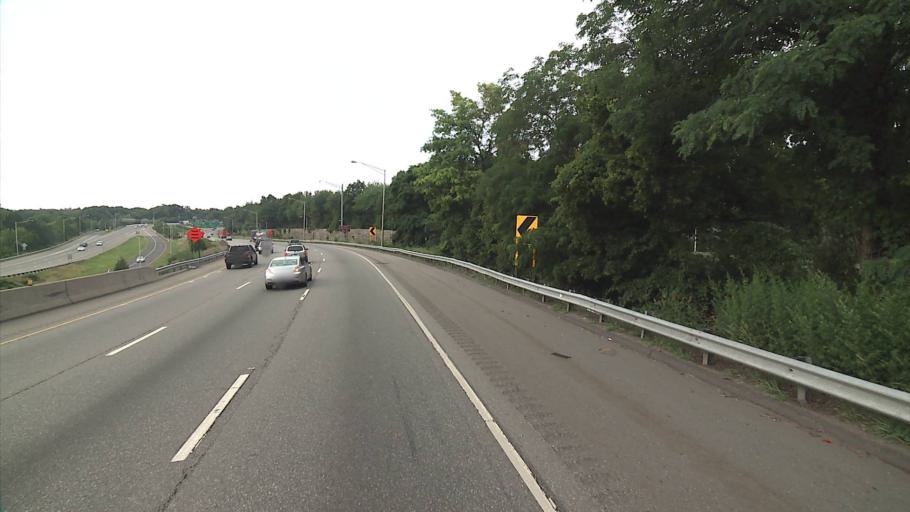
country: US
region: Connecticut
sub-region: Hartford County
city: West Hartford
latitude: 41.7474
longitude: -72.7355
